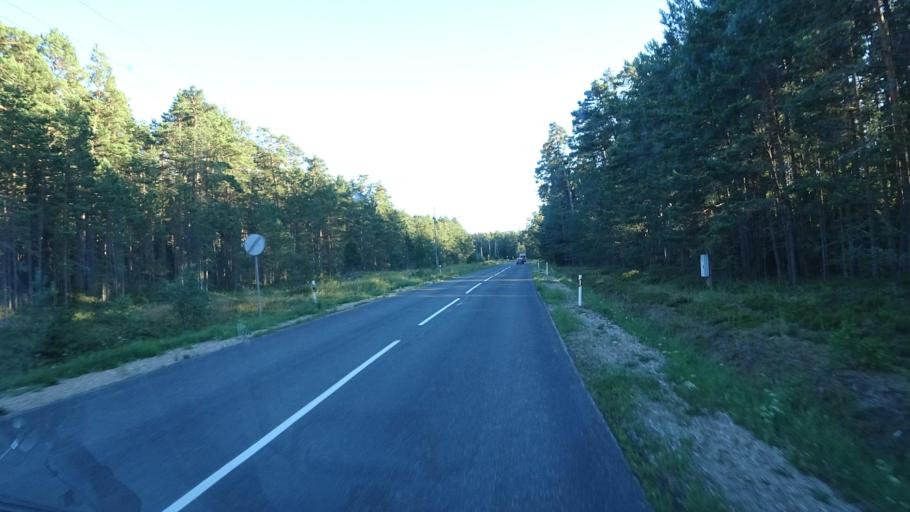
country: LV
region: Dundaga
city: Dundaga
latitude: 57.6821
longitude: 22.5694
